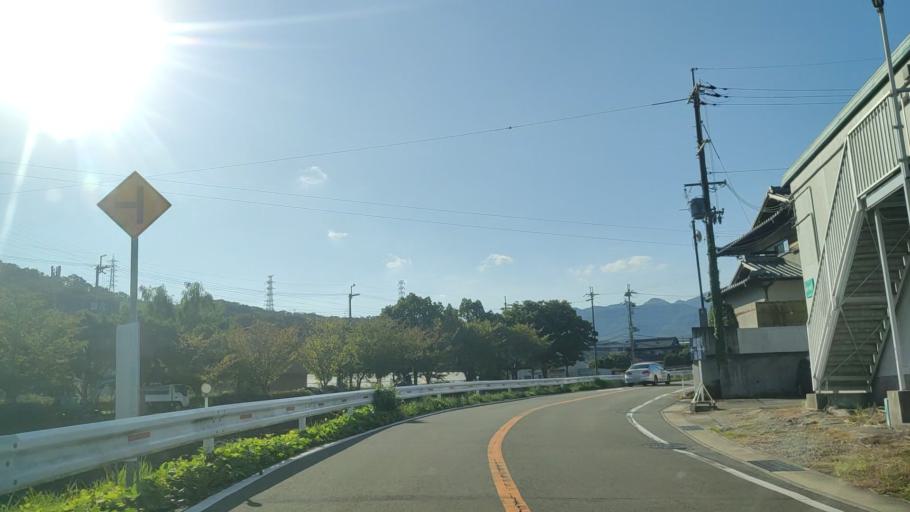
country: JP
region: Hyogo
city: Sandacho
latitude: 34.8229
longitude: 135.2465
